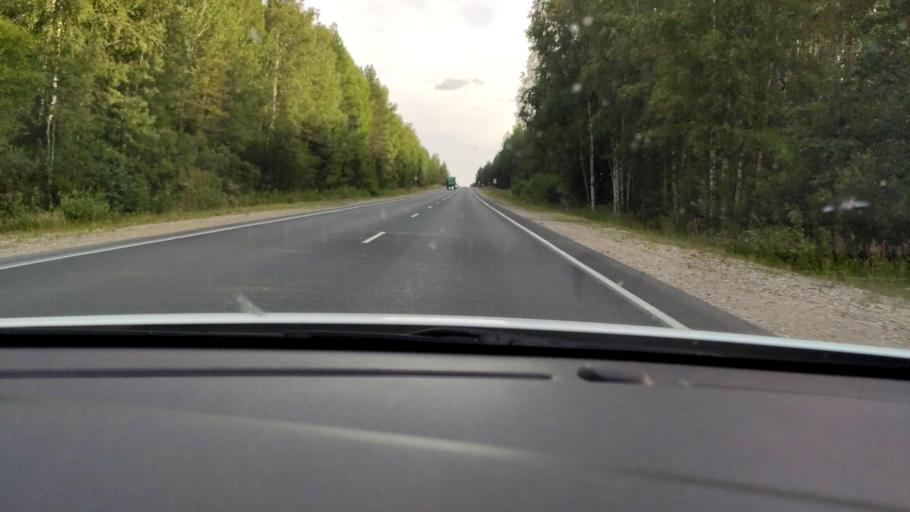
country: RU
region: Mariy-El
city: Suslonger
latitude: 56.2567
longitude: 48.2325
